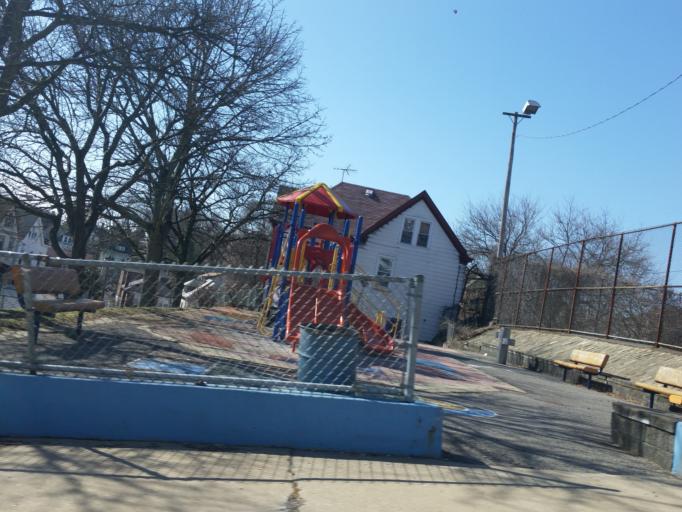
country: US
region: Pennsylvania
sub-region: Allegheny County
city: Crafton
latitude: 40.4395
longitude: -80.0558
